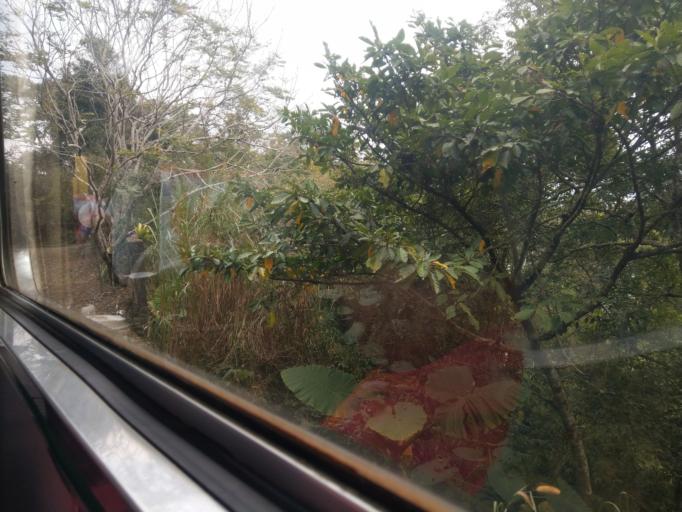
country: TW
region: Taiwan
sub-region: Chiayi
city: Jiayi Shi
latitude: 23.5410
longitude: 120.6205
